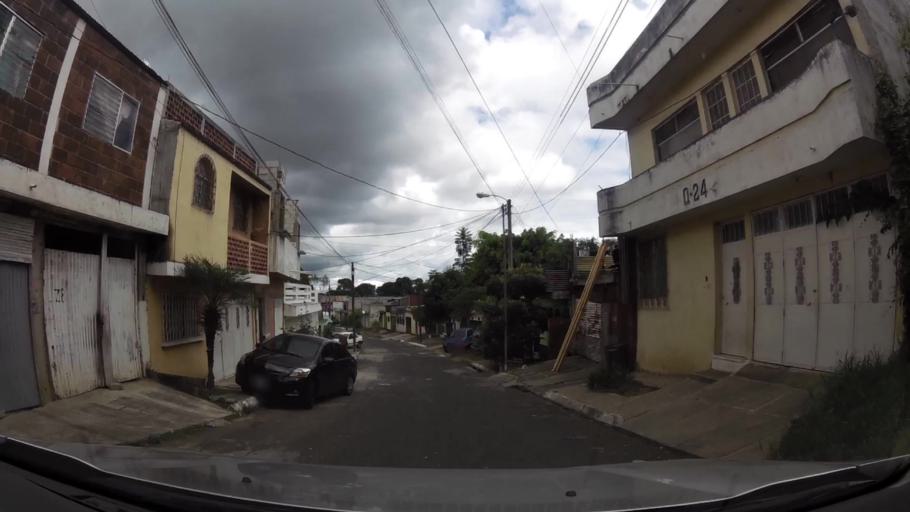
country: GT
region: Guatemala
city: Chinautla
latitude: 14.6841
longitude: -90.5527
